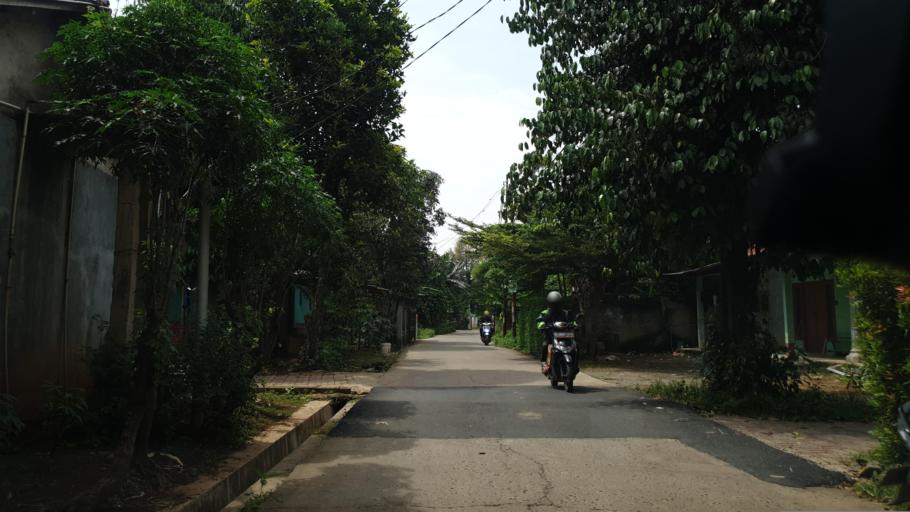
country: ID
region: West Java
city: Sawangan
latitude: -6.3688
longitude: 106.7635
